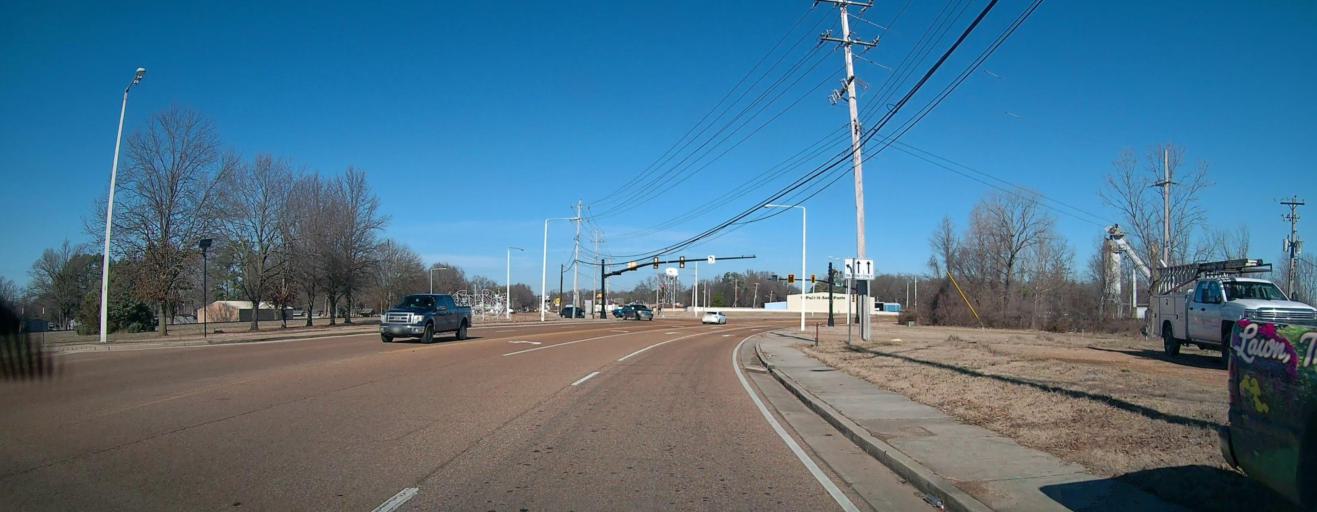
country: US
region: Tennessee
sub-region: Shelby County
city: Millington
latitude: 35.3345
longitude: -89.8982
